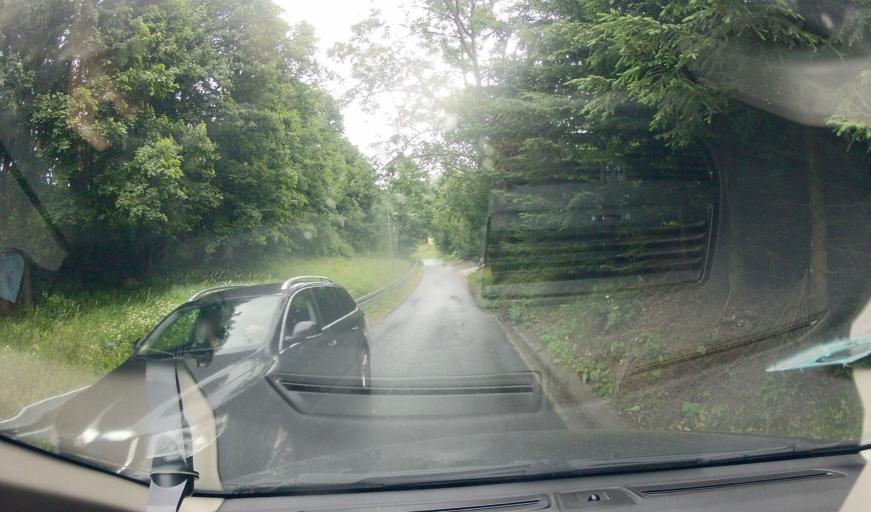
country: PL
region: Lower Silesian Voivodeship
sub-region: Powiat klodzki
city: Miedzylesie
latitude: 50.1200
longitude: 16.6386
